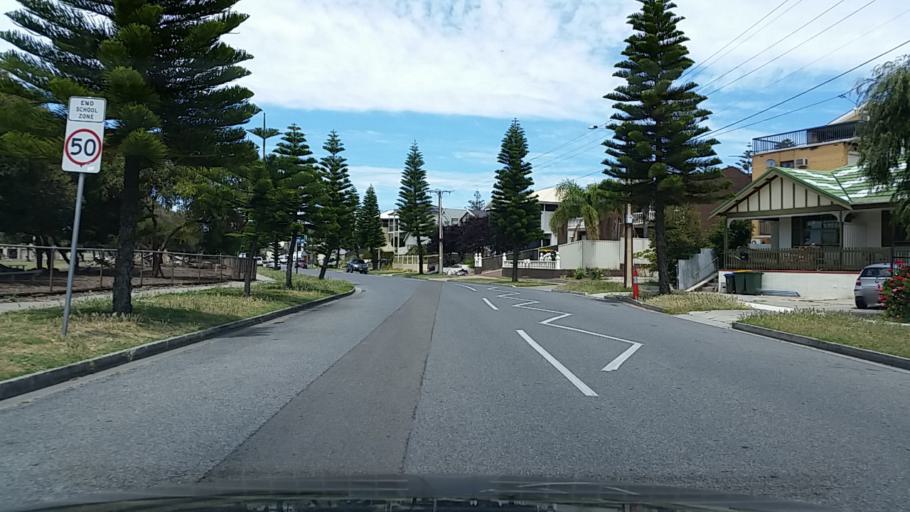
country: AU
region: South Australia
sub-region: Charles Sturt
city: Henley Beach
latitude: -34.9294
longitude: 138.4984
